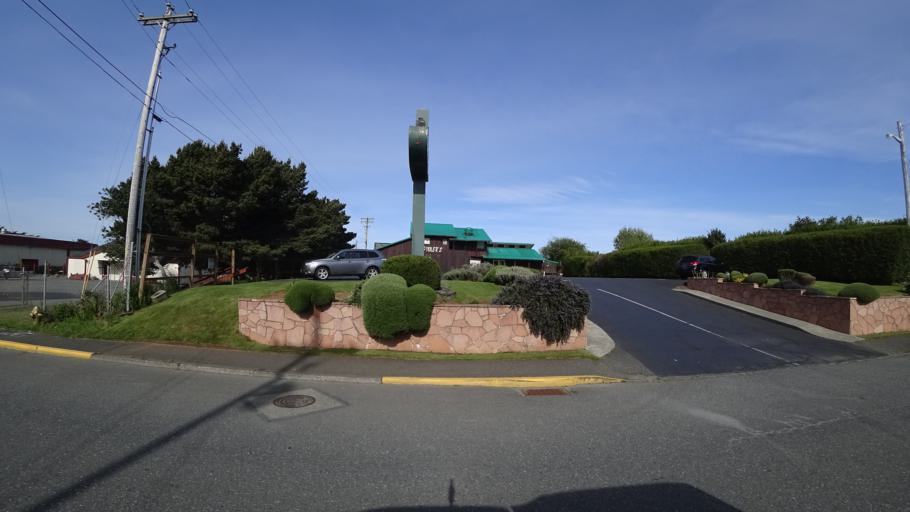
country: US
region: Oregon
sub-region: Curry County
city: Gold Beach
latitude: 42.4064
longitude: -124.4211
